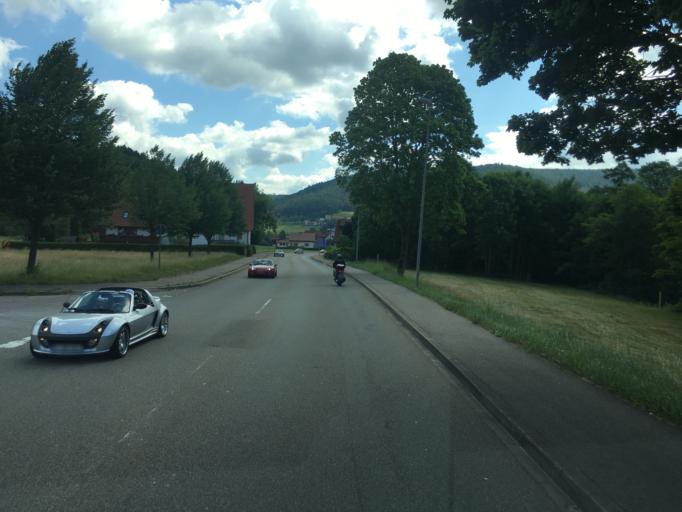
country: DE
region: Baden-Wuerttemberg
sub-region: Karlsruhe Region
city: Baiersbronn
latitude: 48.5095
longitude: 8.3608
